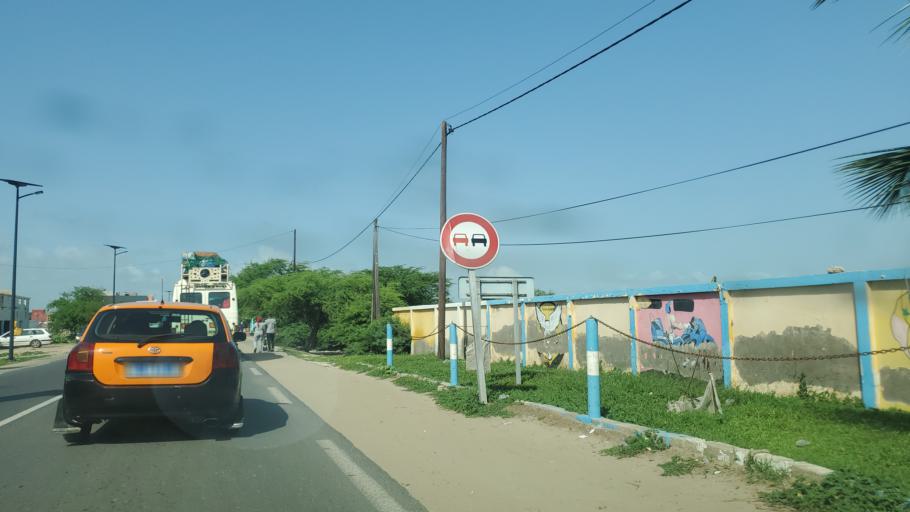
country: SN
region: Saint-Louis
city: Saint-Louis
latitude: 16.0290
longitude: -16.4749
